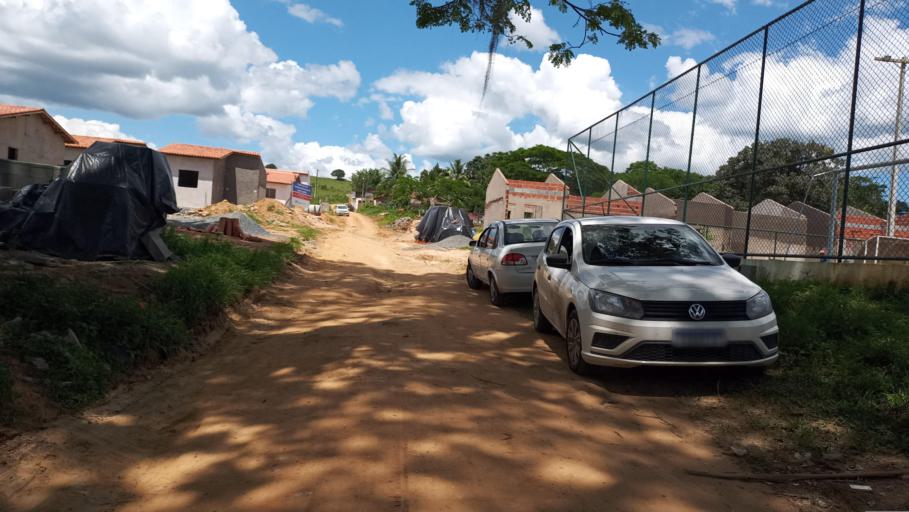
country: BR
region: Bahia
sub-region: Ubata
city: Ubata
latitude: -14.2098
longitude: -39.5368
